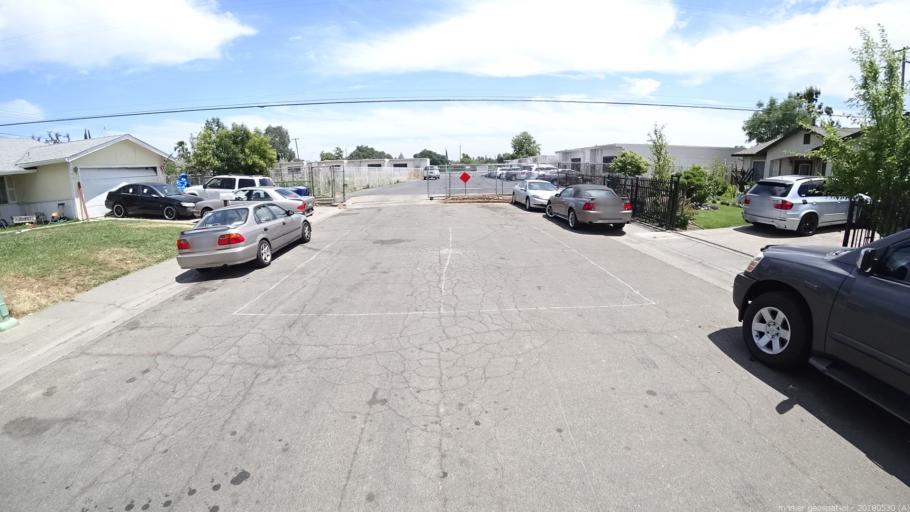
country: US
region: California
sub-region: Sacramento County
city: Sacramento
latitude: 38.6272
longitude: -121.4626
